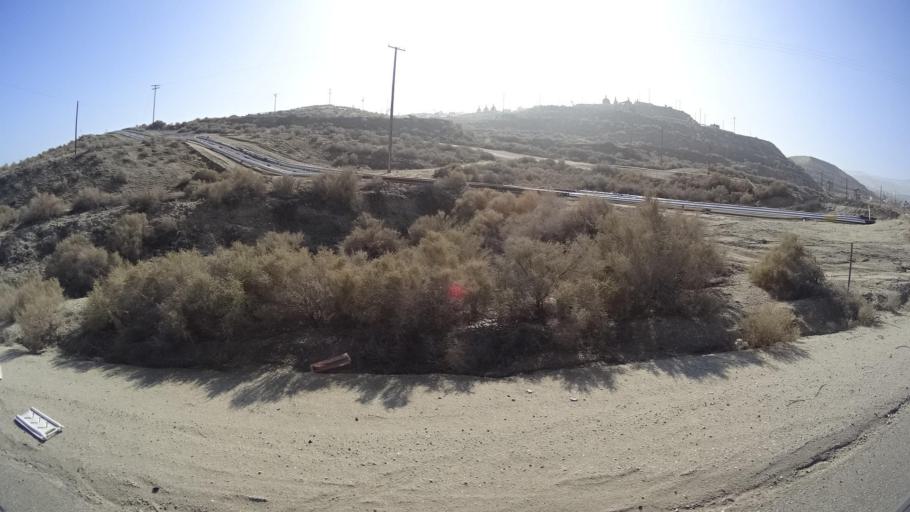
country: US
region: California
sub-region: Kern County
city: Taft Heights
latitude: 35.1388
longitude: -119.5030
